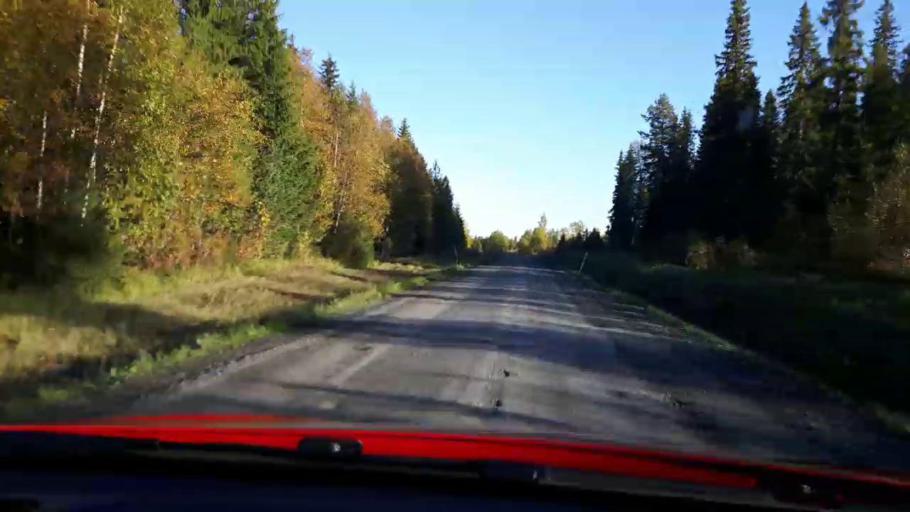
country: SE
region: Jaemtland
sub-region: OEstersunds Kommun
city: Lit
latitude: 63.6677
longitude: 14.7066
